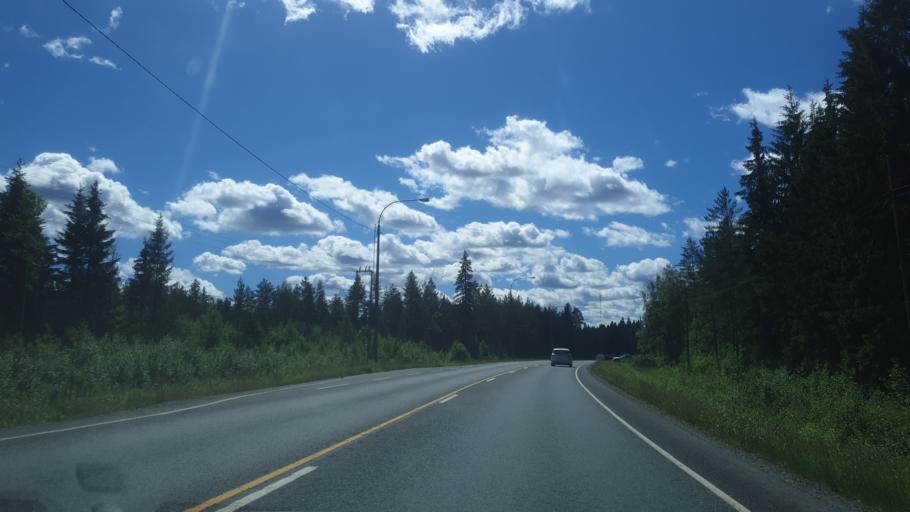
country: FI
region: Northern Savo
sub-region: Varkaus
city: Leppaevirta
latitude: 62.5616
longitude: 27.6214
